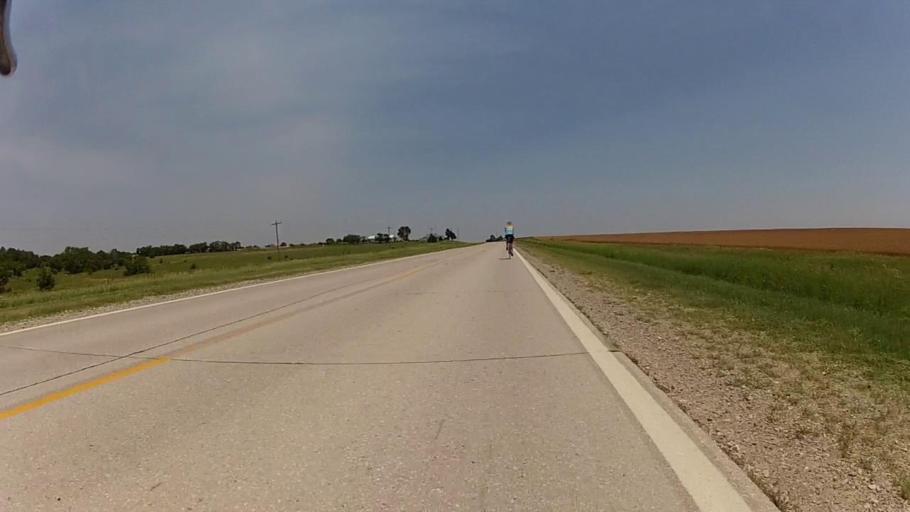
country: US
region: Kansas
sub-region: Sumner County
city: Wellington
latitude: 37.0569
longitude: -97.3080
